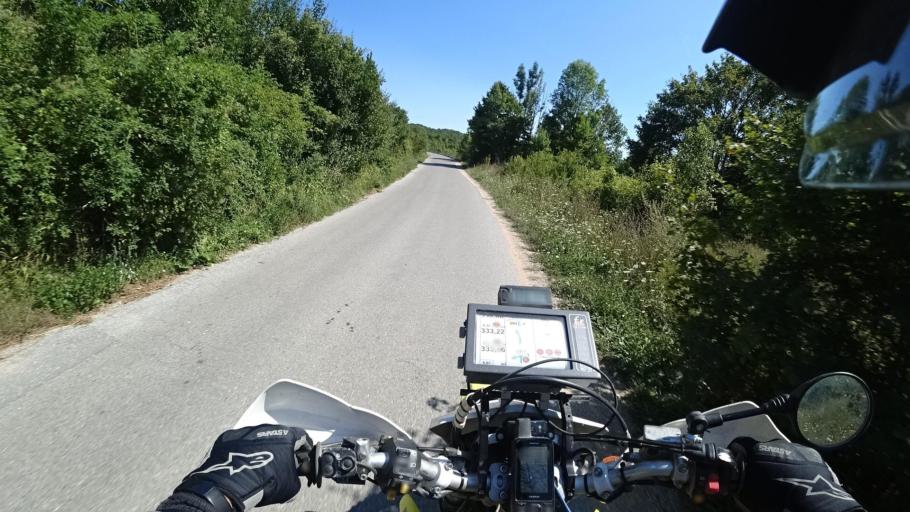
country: HR
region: Licko-Senjska
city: Popovaca
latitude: 44.7306
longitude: 15.2806
